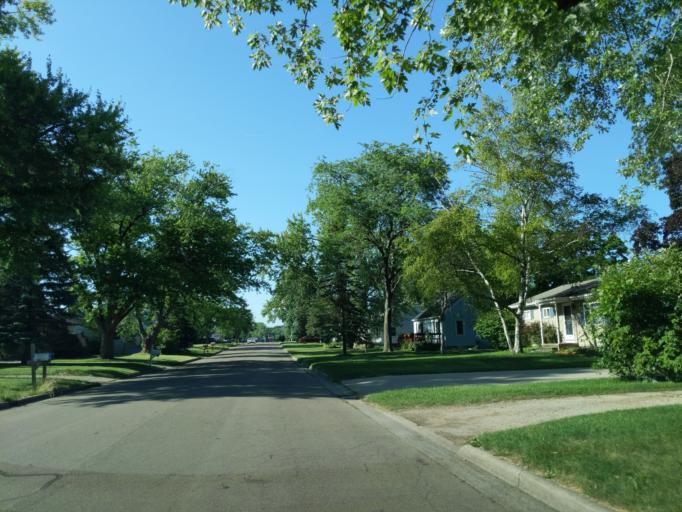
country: US
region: Michigan
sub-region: Eaton County
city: Waverly
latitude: 42.7388
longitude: -84.6195
